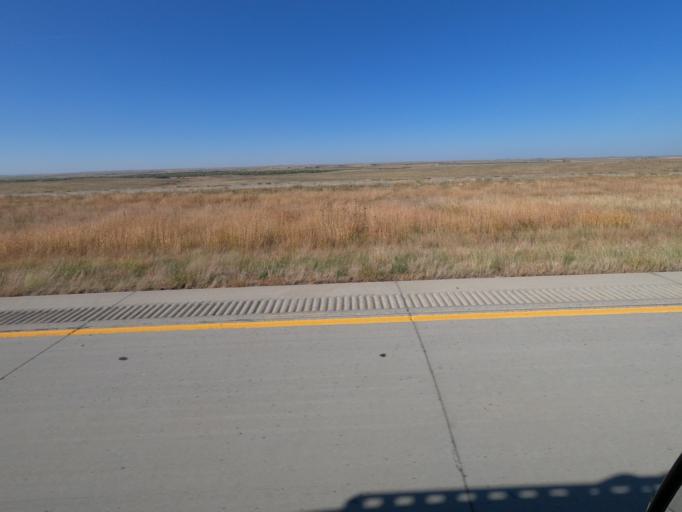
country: US
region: Nebraska
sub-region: Deuel County
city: Chappell
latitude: 40.9106
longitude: -102.4928
